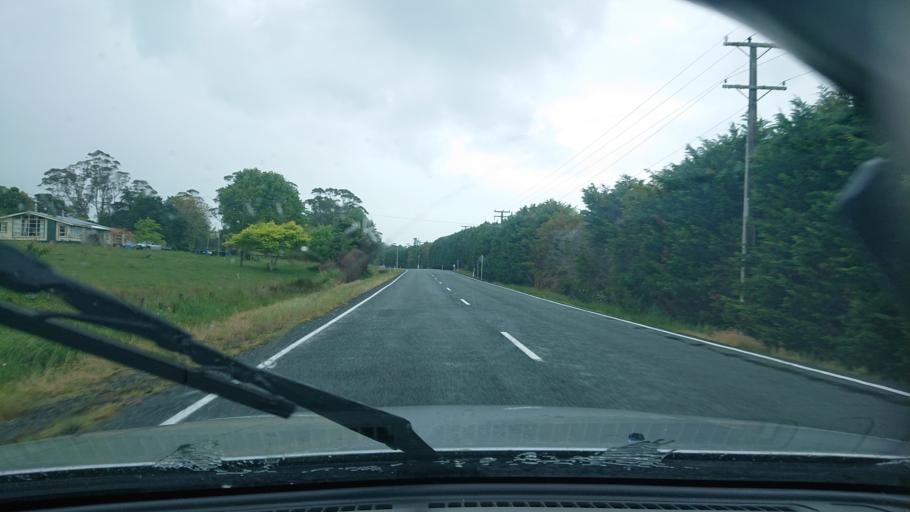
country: NZ
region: Auckland
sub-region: Auckland
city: Wellsford
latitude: -36.3225
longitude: 174.4816
